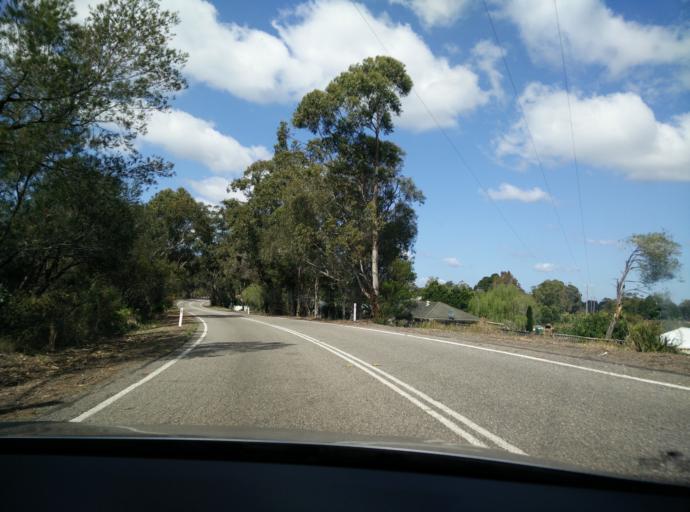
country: AU
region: New South Wales
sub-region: Gosford Shire
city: Point Clare
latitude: -33.4446
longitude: 151.2928
